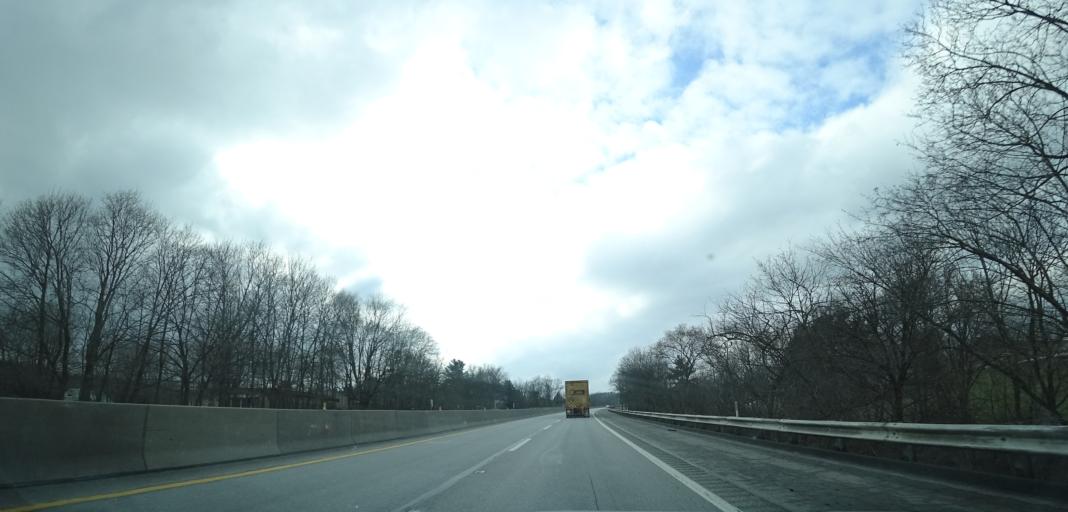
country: US
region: Pennsylvania
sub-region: Beaver County
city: Beaver Falls
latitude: 40.7906
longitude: -80.2679
